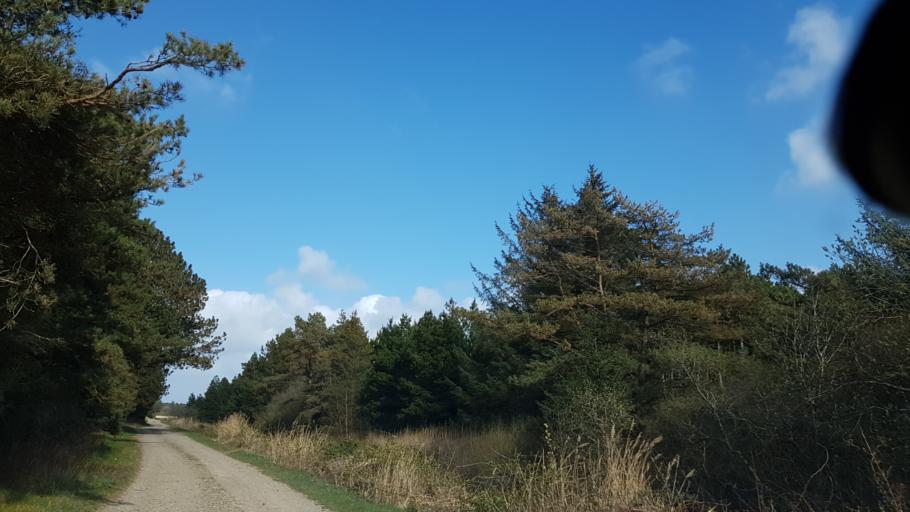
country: DE
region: Schleswig-Holstein
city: List
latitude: 55.0837
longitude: 8.5341
